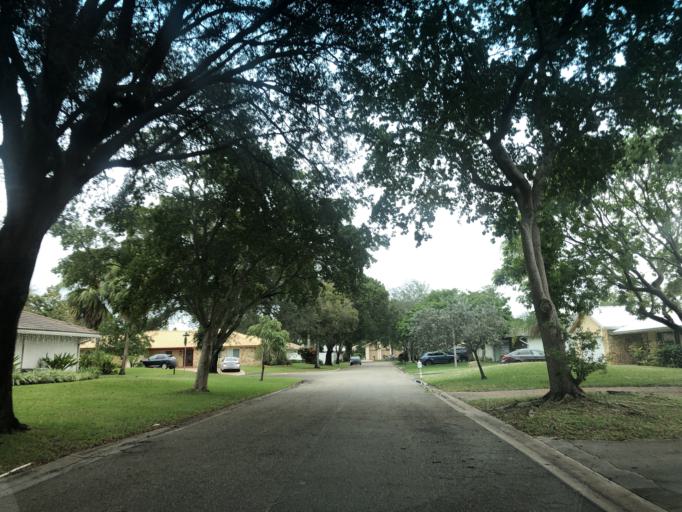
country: US
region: Florida
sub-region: Broward County
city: North Lauderdale
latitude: 26.2314
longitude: -80.2345
